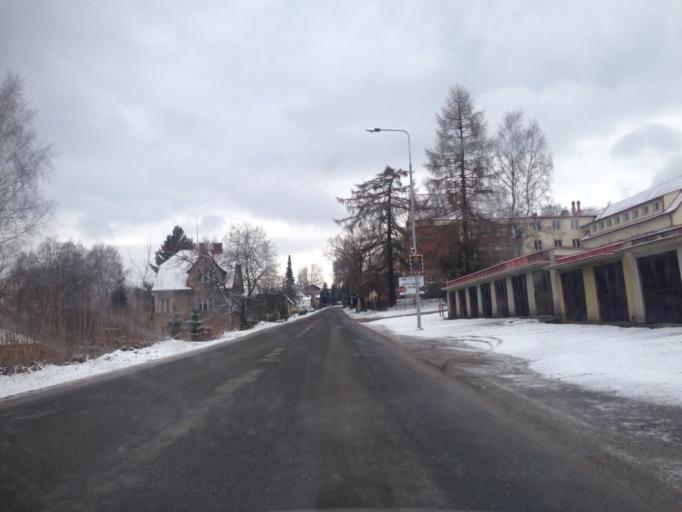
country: CZ
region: Liberecky
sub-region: Okres Semily
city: Vysoke nad Jizerou
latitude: 50.6802
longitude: 15.4069
